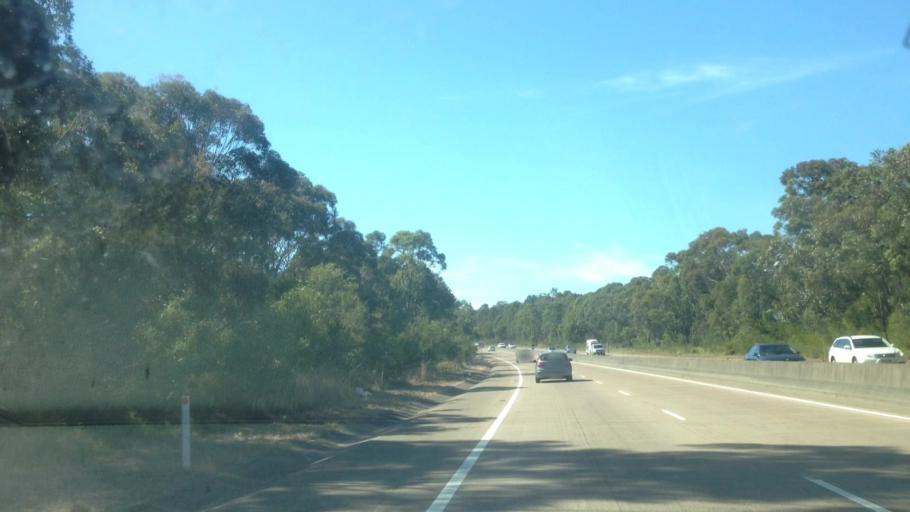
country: AU
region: New South Wales
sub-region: Lake Macquarie Shire
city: Holmesville
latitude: -32.9005
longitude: 151.6146
